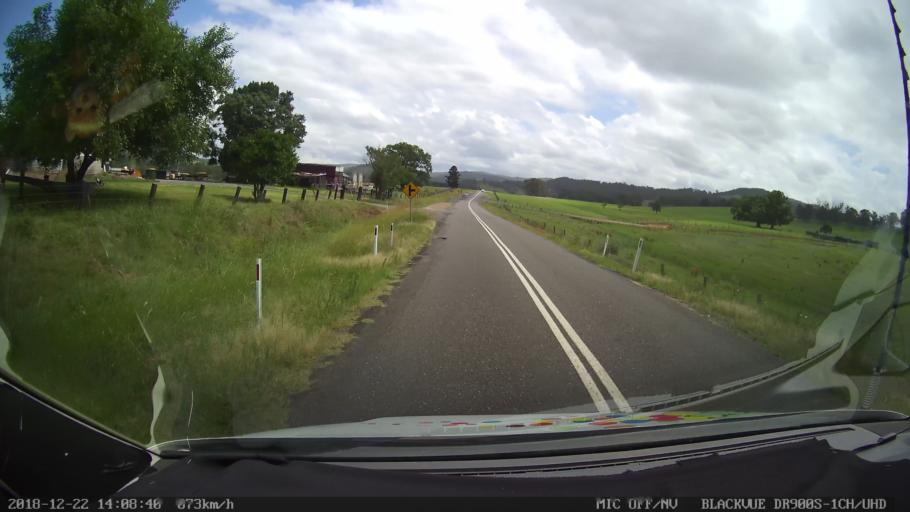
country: AU
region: New South Wales
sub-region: Clarence Valley
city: Coutts Crossing
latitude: -29.9805
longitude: 152.7239
